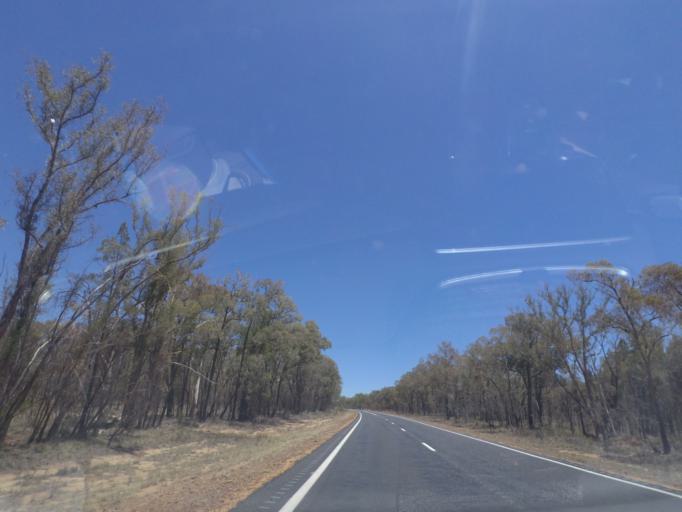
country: AU
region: New South Wales
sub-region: Warrumbungle Shire
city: Coonabarabran
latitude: -31.1769
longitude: 149.3575
